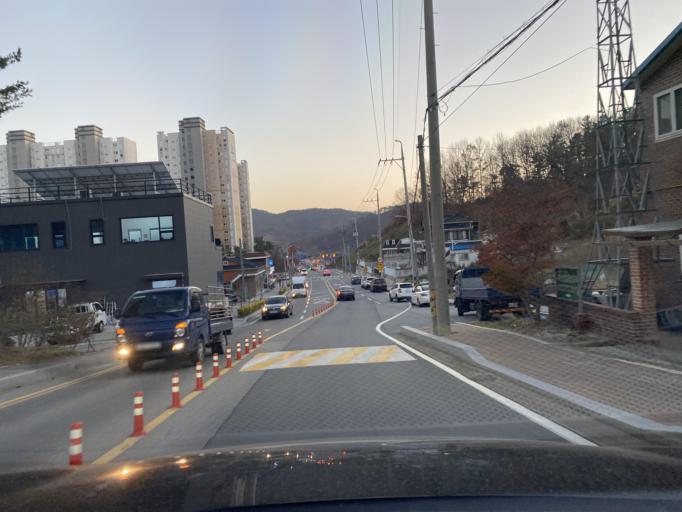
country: KR
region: Chungcheongnam-do
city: Yesan
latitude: 36.6842
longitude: 126.8438
